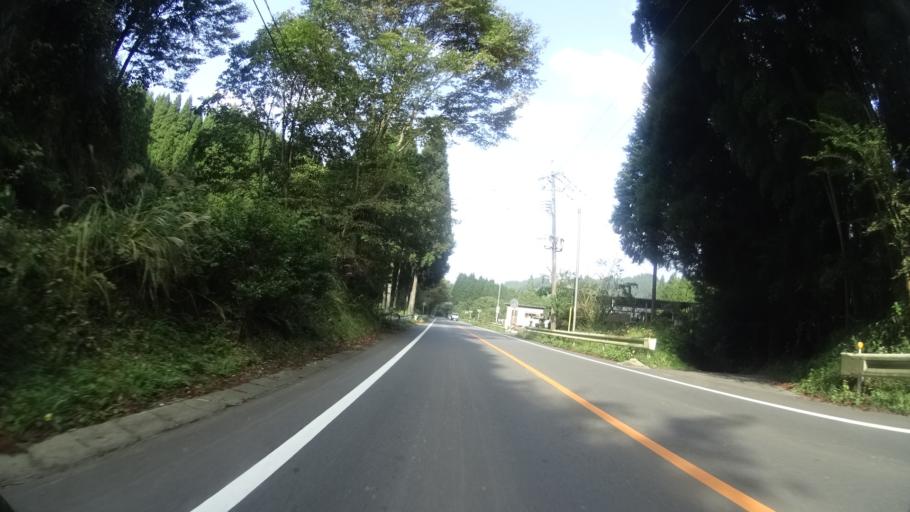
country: JP
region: Kumamoto
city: Aso
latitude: 33.0842
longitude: 131.0656
